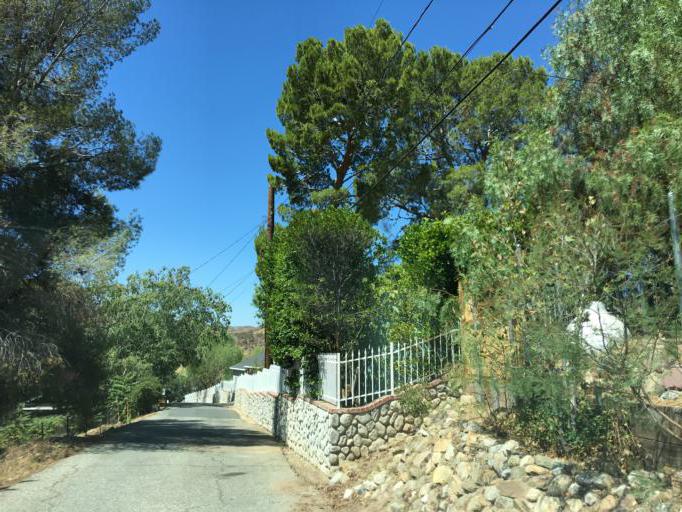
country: US
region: California
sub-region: Los Angeles County
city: Agua Dulce
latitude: 34.5094
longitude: -118.3674
